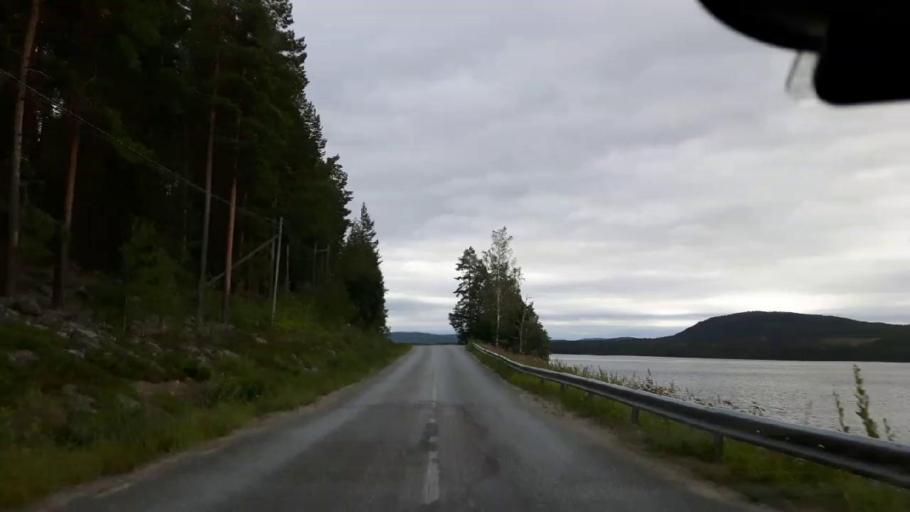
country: SE
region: Jaemtland
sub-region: Braecke Kommun
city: Braecke
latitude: 62.8656
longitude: 15.6179
